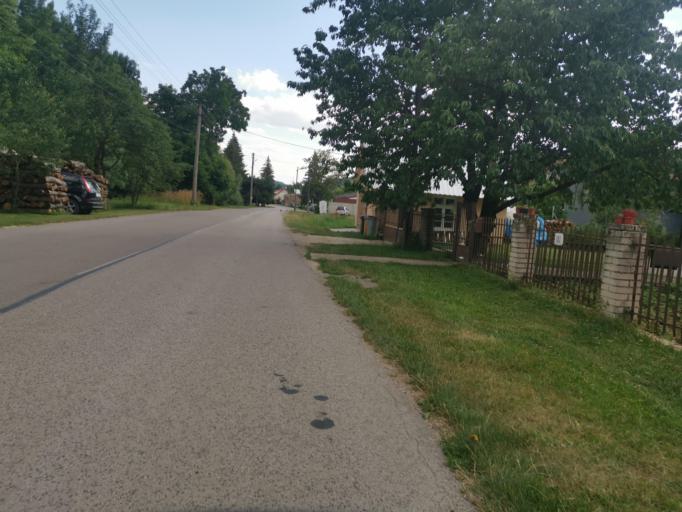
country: CZ
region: South Moravian
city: Knezdub
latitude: 48.8004
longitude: 17.4112
